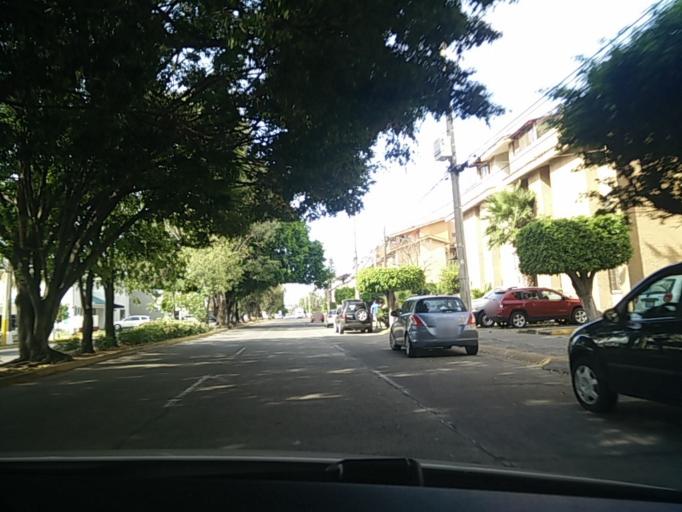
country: MX
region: Jalisco
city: Guadalajara
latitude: 20.6828
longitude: -103.3870
